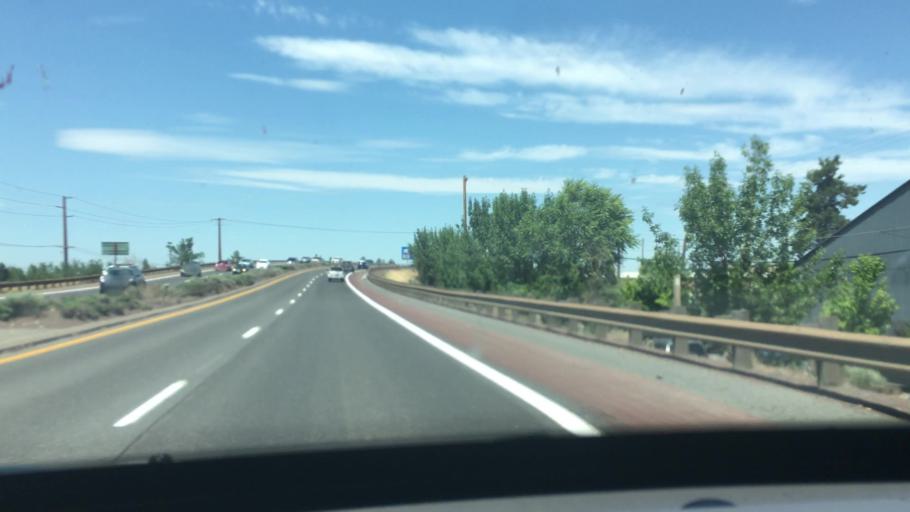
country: US
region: Oregon
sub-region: Deschutes County
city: Bend
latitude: 44.0739
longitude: -121.3040
